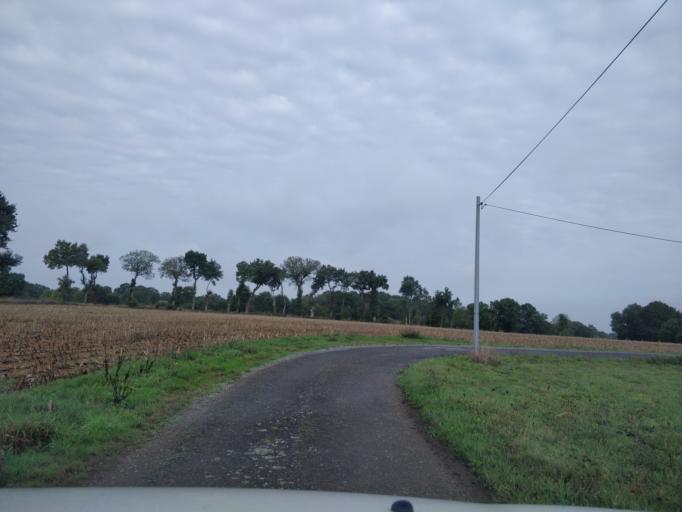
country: FR
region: Brittany
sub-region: Departement d'Ille-et-Vilaine
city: Liffre
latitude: 48.2143
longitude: -1.4793
